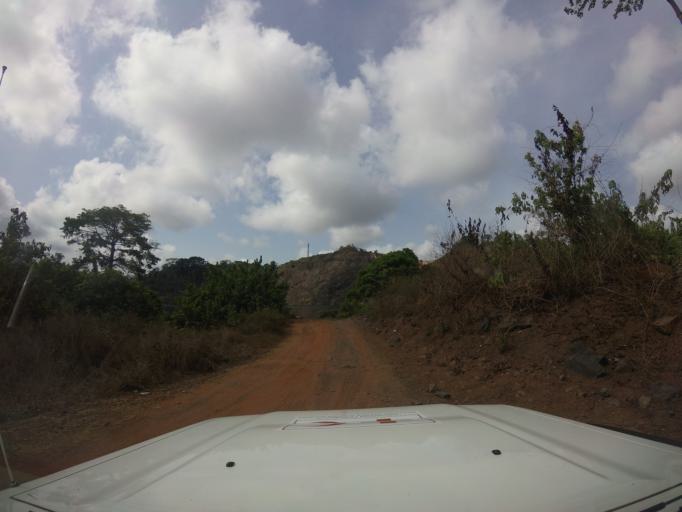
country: LR
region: Bomi
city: Tubmanburg
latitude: 6.8998
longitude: -10.8266
